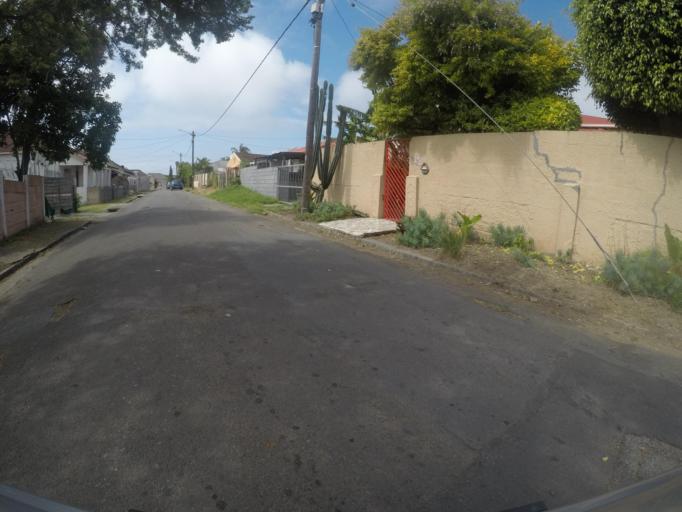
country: ZA
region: Eastern Cape
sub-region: Buffalo City Metropolitan Municipality
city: East London
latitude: -32.9975
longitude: 27.9083
